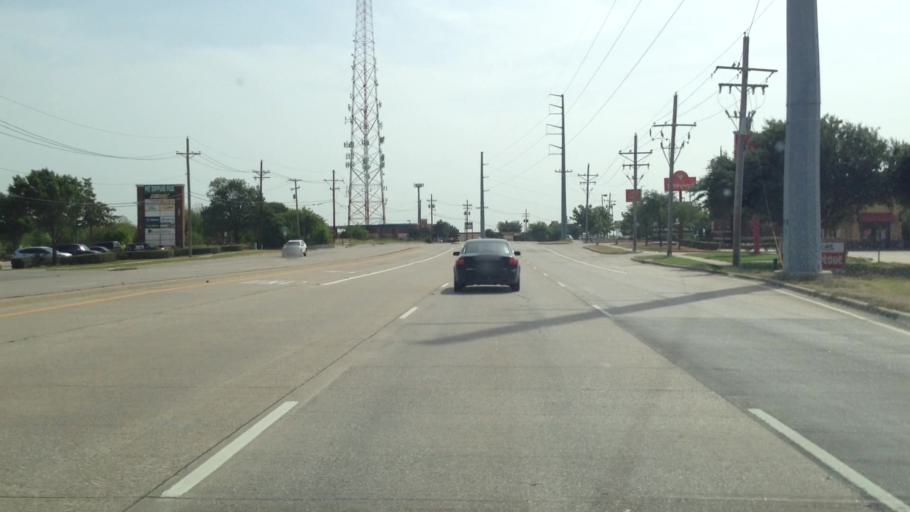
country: US
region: Texas
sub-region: Denton County
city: Lewisville
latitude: 33.0039
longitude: -96.9865
